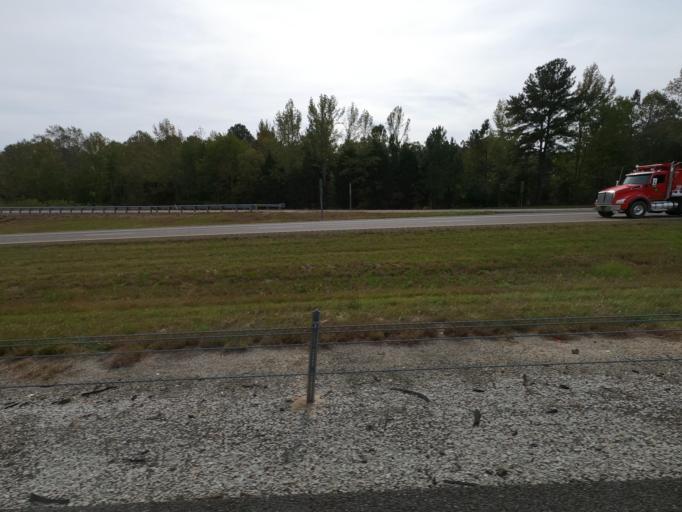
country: US
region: Tennessee
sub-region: Henderson County
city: Lexington
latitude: 35.7543
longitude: -88.5155
